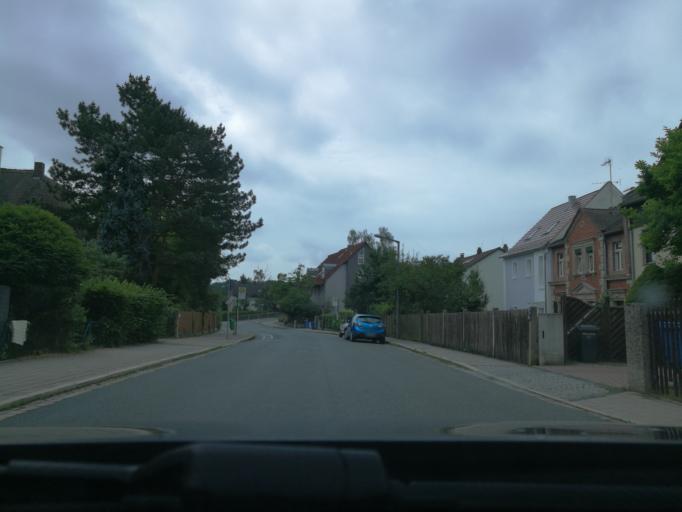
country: DE
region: Bavaria
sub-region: Regierungsbezirk Mittelfranken
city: Furth
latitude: 49.4764
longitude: 10.9713
